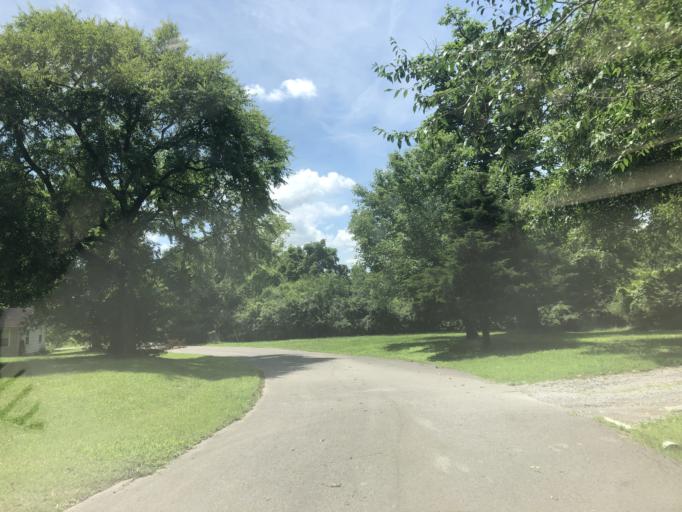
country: US
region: Tennessee
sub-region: Davidson County
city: Lakewood
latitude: 36.2530
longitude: -86.6771
